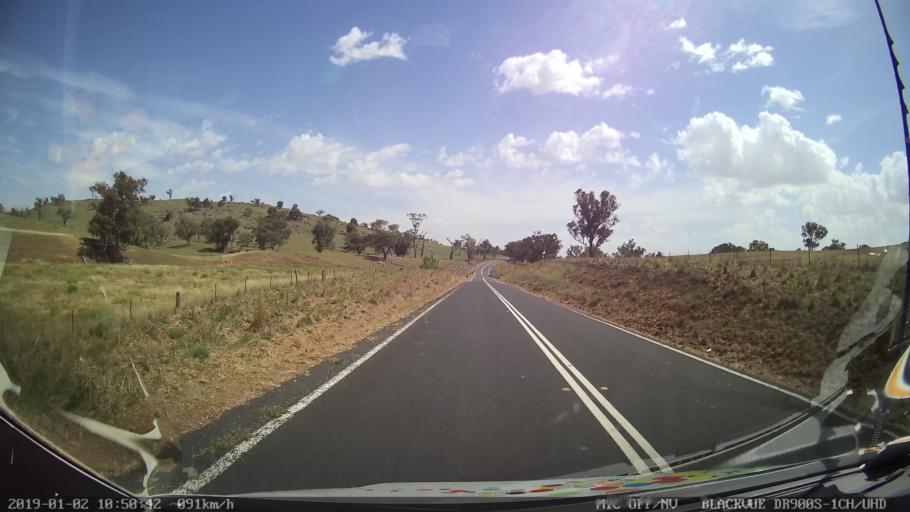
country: AU
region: New South Wales
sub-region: Cootamundra
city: Cootamundra
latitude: -34.7109
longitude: 148.2757
